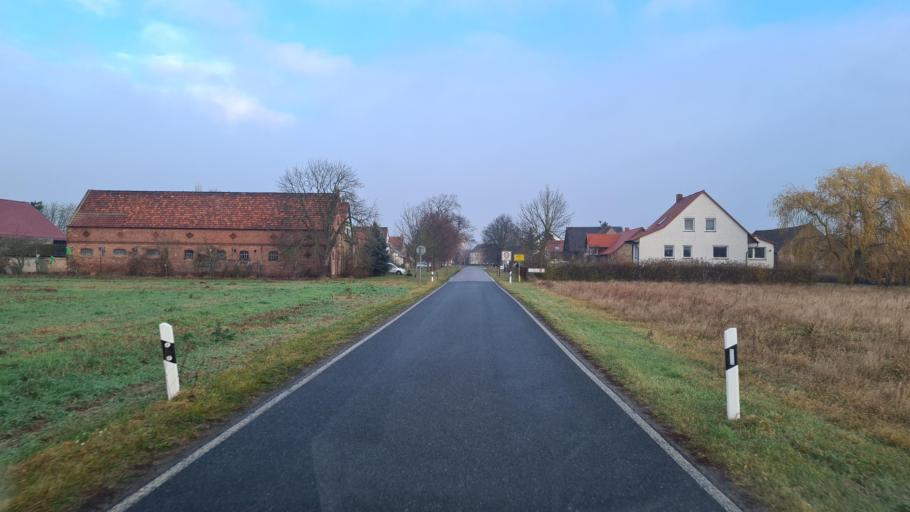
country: DE
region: Brandenburg
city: Beelitz
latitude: 52.1541
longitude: 12.9687
